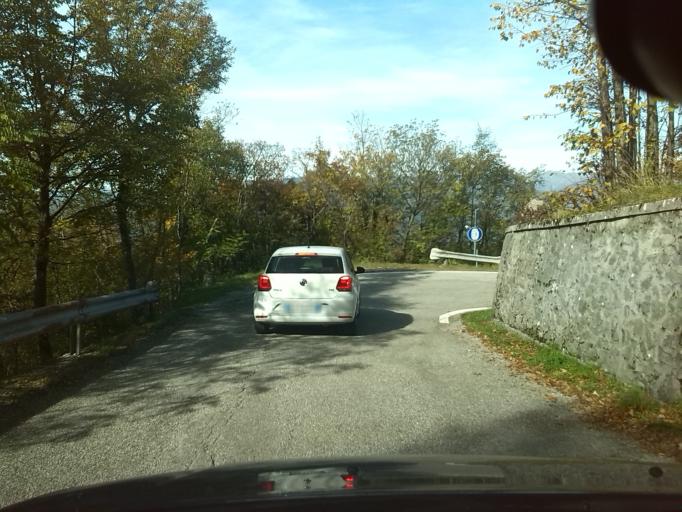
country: IT
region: Friuli Venezia Giulia
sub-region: Provincia di Udine
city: San Leonardo
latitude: 46.0950
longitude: 13.5187
